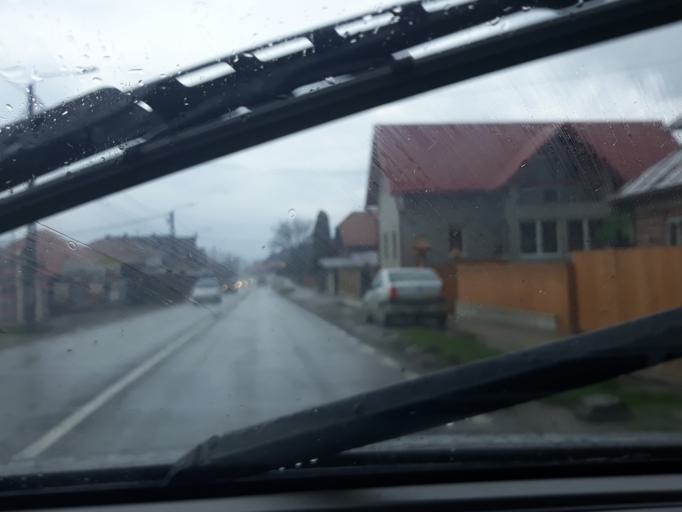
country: RO
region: Harghita
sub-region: Comuna Corund
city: Corund
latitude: 46.4751
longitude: 25.1774
